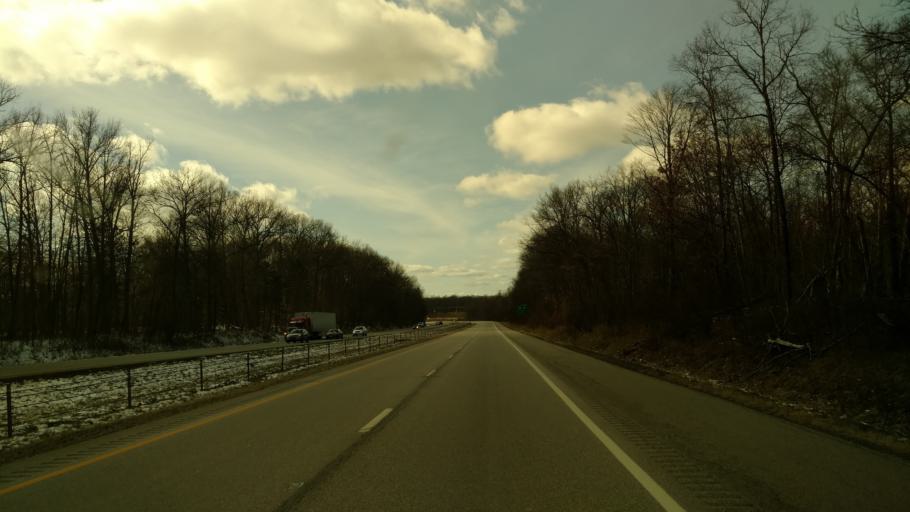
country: US
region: Ohio
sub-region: Portage County
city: Ravenna
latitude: 41.1086
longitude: -81.2257
